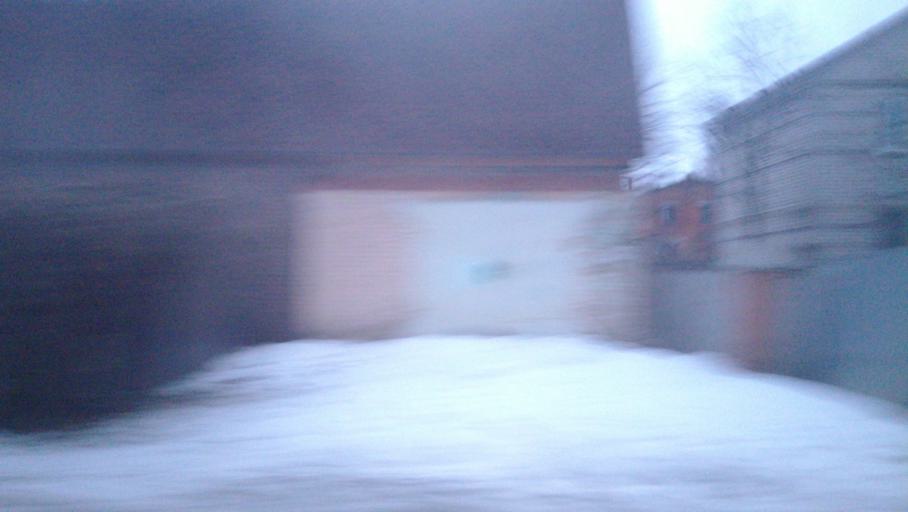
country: RU
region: Tula
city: Tula
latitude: 54.1999
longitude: 37.5400
